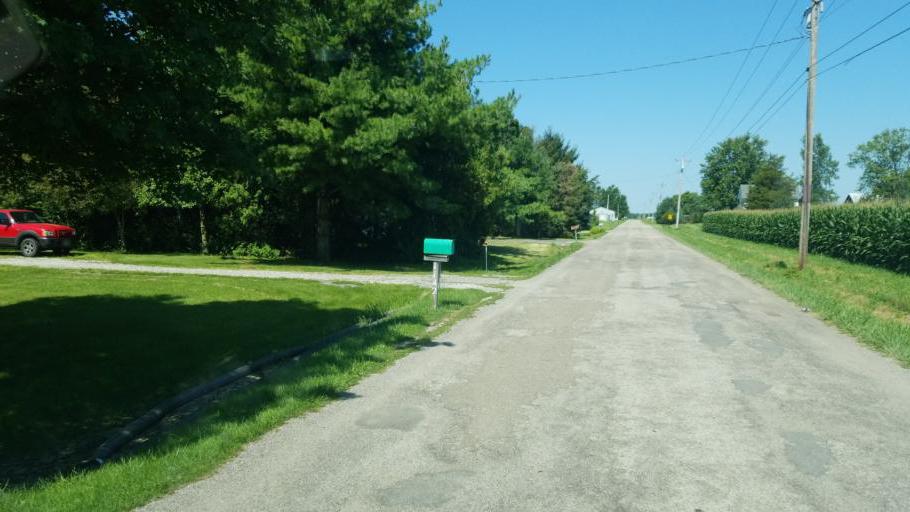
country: US
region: Ohio
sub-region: Delaware County
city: Ashley
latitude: 40.4291
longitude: -82.9652
